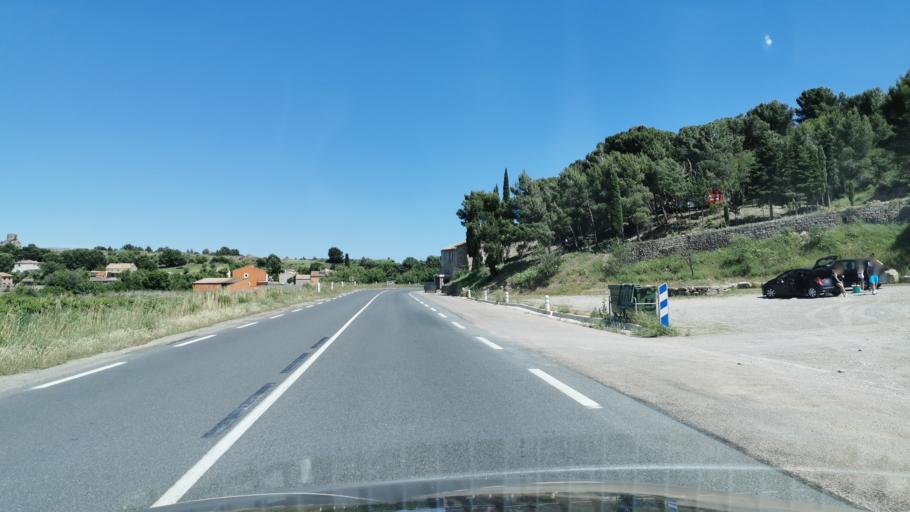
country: FR
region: Languedoc-Roussillon
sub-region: Departement de l'Aude
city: Nevian
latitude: 43.1855
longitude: 2.9257
